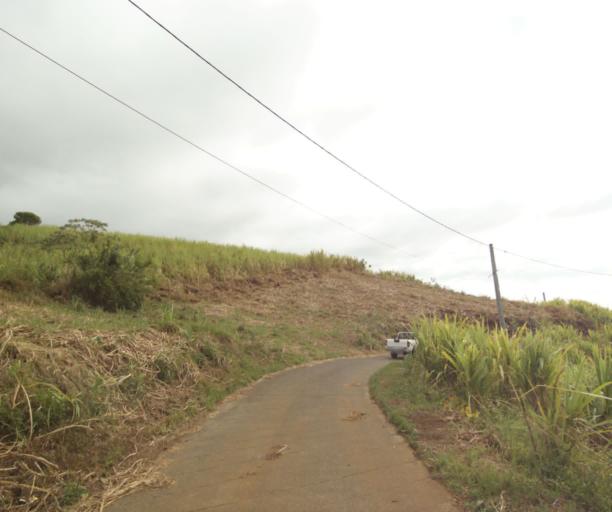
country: RE
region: Reunion
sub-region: Reunion
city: Saint-Paul
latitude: -21.0062
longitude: 55.3488
